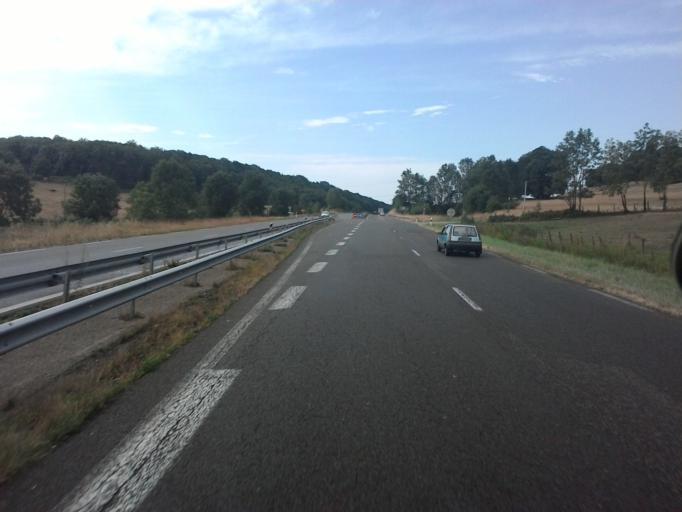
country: FR
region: Franche-Comte
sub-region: Departement du Jura
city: Lons-le-Saunier
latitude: 46.7202
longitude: 5.5571
